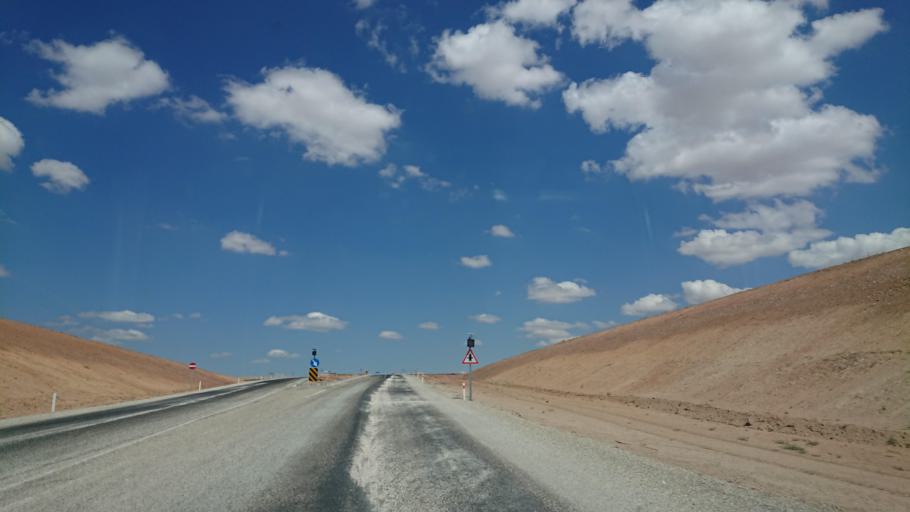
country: TR
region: Aksaray
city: Sariyahsi
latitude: 39.1232
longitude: 33.9674
